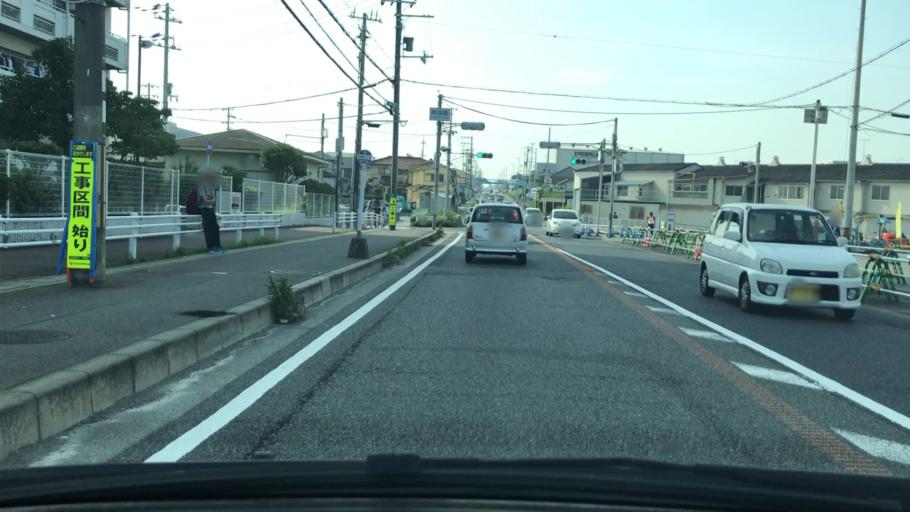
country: JP
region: Hyogo
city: Kakogawacho-honmachi
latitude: 34.7122
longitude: 134.9014
